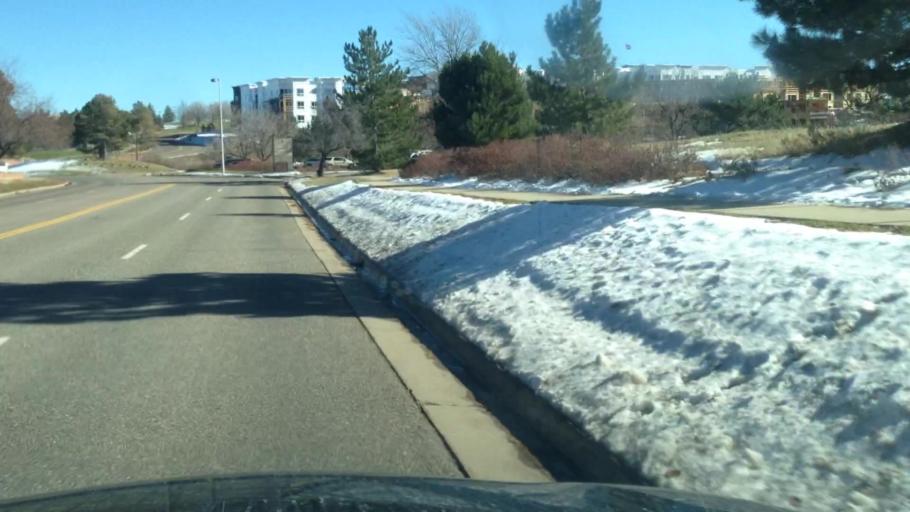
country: US
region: Colorado
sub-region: Douglas County
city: Meridian
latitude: 39.5647
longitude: -104.8627
